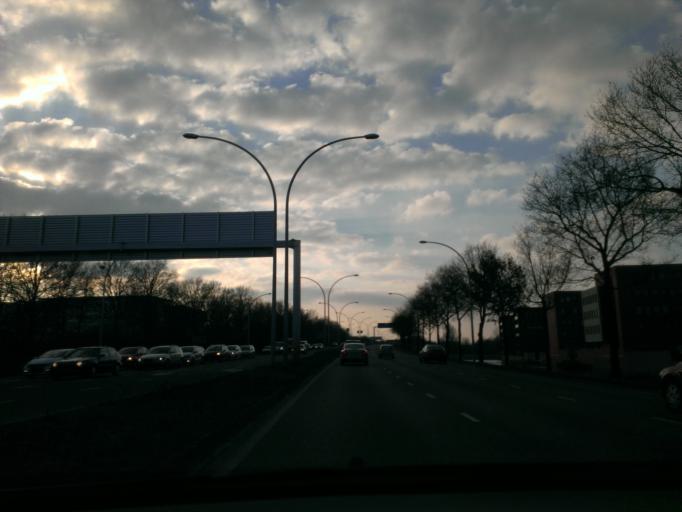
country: NL
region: Overijssel
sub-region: Gemeente Zwolle
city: Zwolle
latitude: 52.5015
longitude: 6.0831
